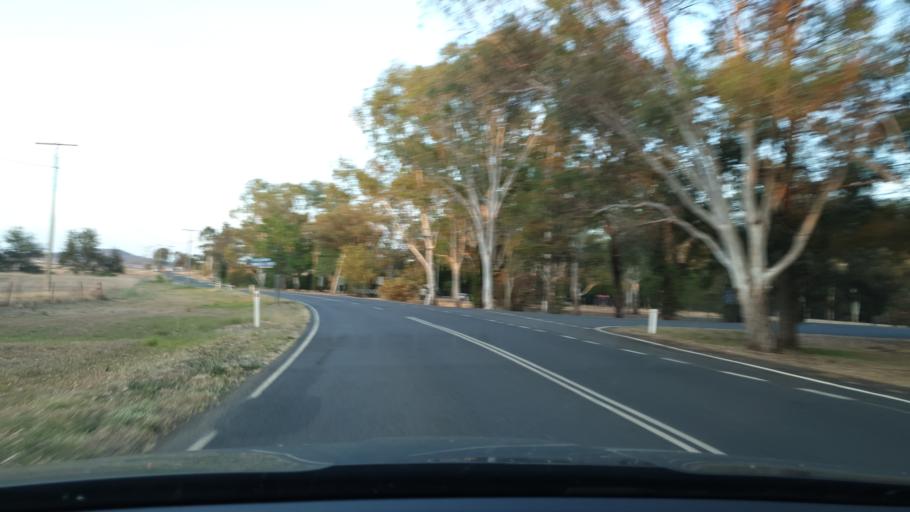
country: AU
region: Queensland
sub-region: Southern Downs
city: Warwick
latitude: -28.0298
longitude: 151.9823
